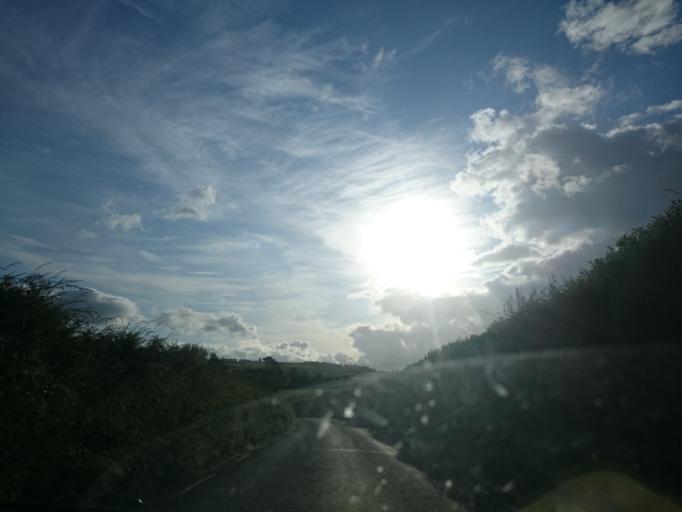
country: IE
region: Leinster
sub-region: Loch Garman
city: New Ross
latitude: 52.4094
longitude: -7.0045
